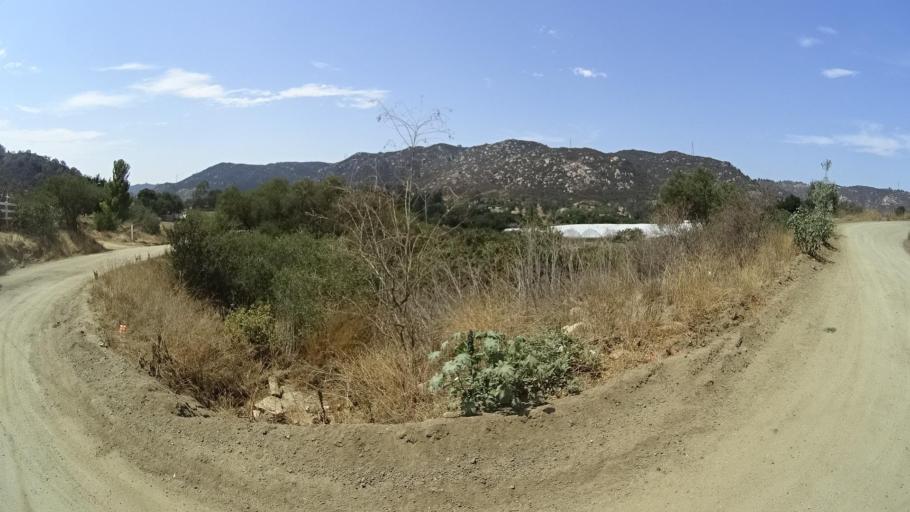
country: US
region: California
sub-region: San Diego County
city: Hidden Meadows
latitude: 33.1984
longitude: -117.0845
